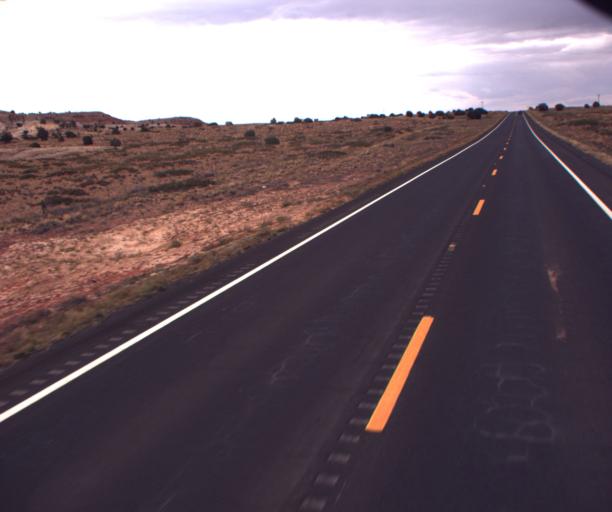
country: US
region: Arizona
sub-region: Coconino County
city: Tuba City
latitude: 36.2473
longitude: -111.0230
